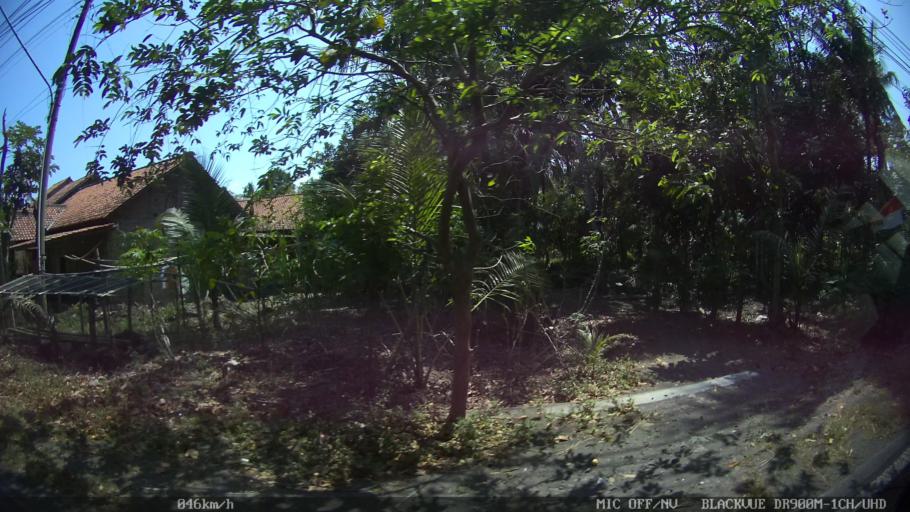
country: ID
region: Daerah Istimewa Yogyakarta
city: Srandakan
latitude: -7.9146
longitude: 110.0976
